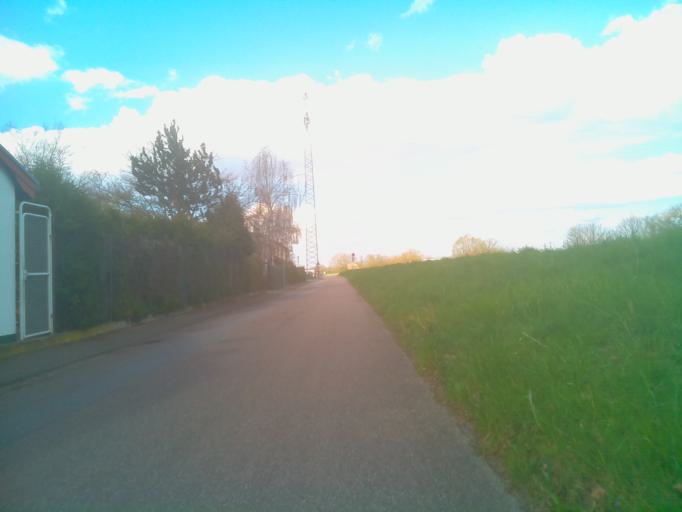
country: DE
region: Baden-Wuerttemberg
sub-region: Karlsruhe Region
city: Ladenburg
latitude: 49.4731
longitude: 8.5916
